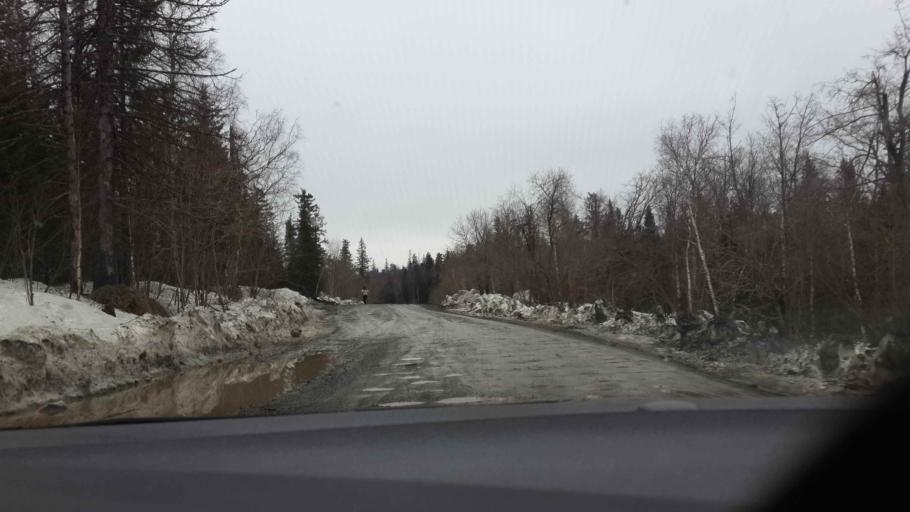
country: RU
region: Chelyabinsk
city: Magnitka
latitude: 55.2713
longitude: 59.6991
